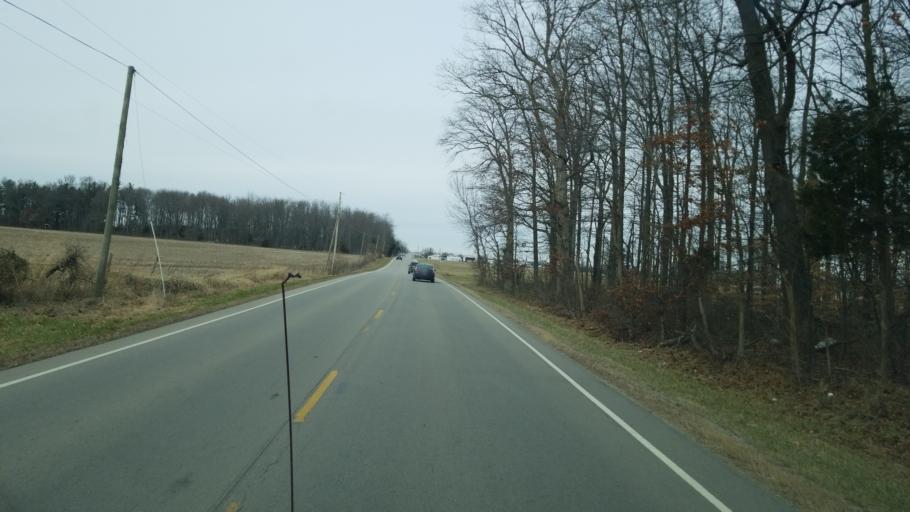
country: US
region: Ohio
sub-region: Adams County
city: Winchester
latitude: 39.0559
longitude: -83.7036
